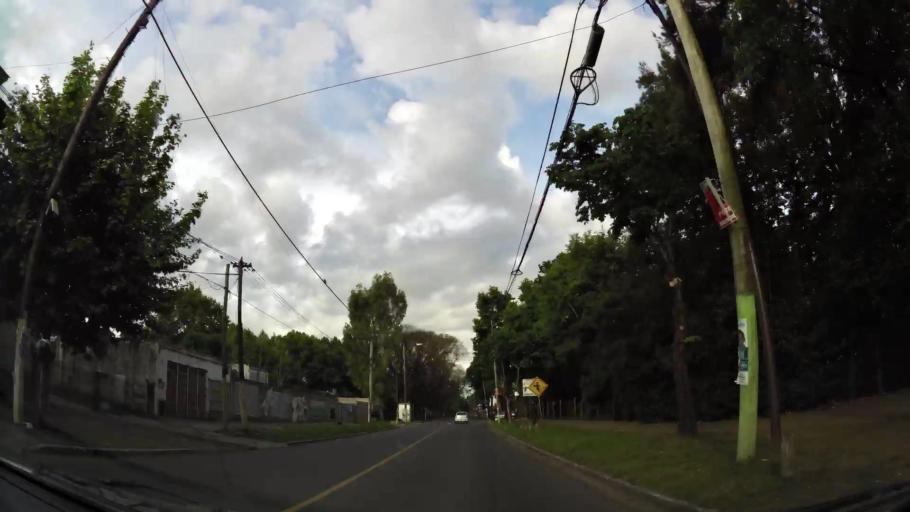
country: AR
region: Buenos Aires
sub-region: Partido de Quilmes
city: Quilmes
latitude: -34.7370
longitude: -58.2593
